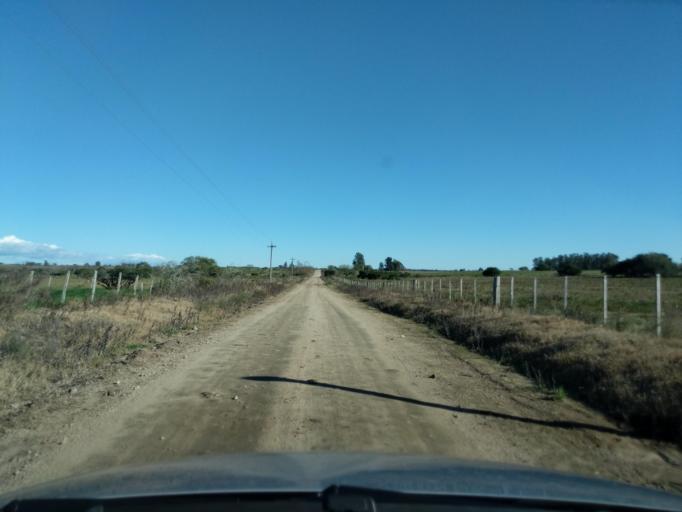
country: UY
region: Florida
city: Florida
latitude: -34.0809
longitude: -56.2579
